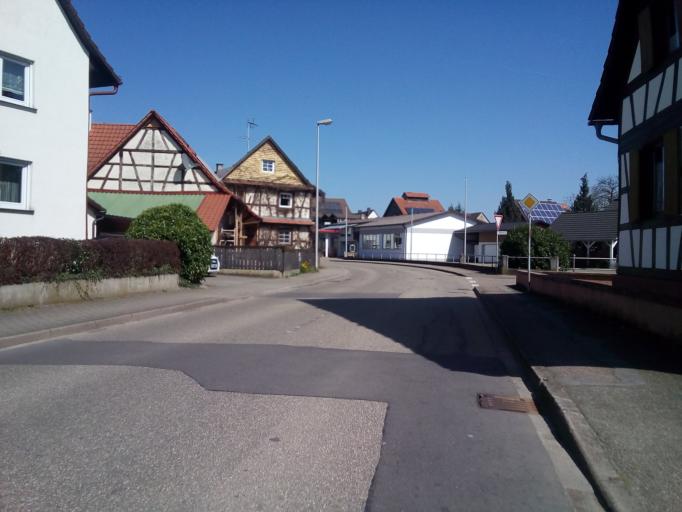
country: FR
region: Alsace
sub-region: Departement du Bas-Rhin
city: La Wantzenau
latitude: 48.6233
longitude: 7.8537
